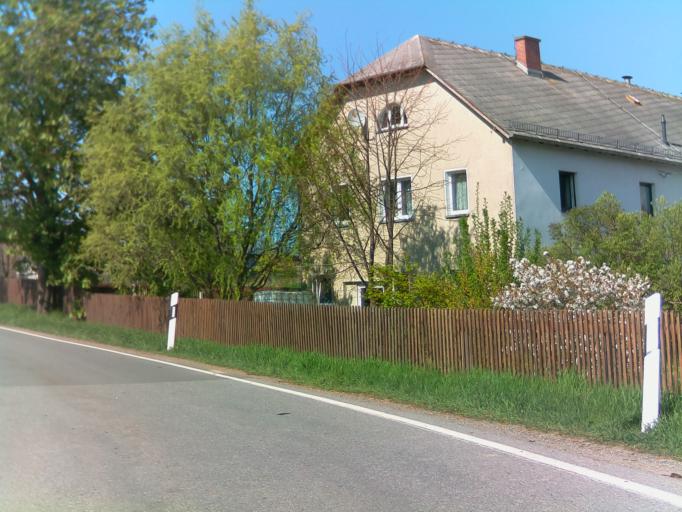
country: DE
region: Saxony
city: Pausa
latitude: 50.5969
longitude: 12.0404
